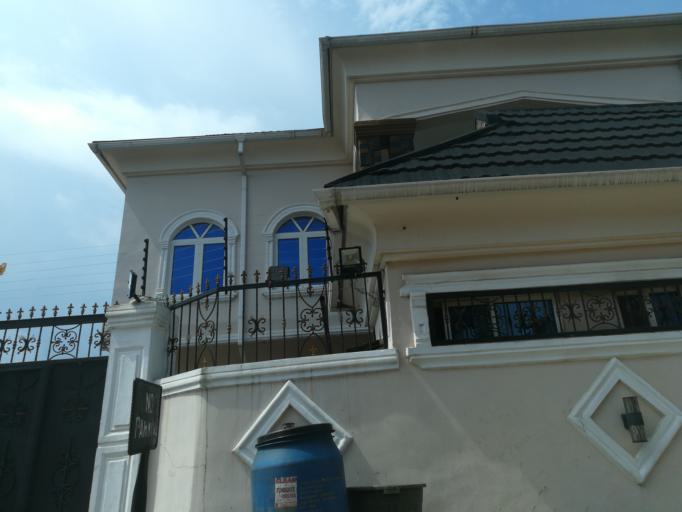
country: NG
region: Lagos
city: Oshodi
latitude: 6.5448
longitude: 3.3208
